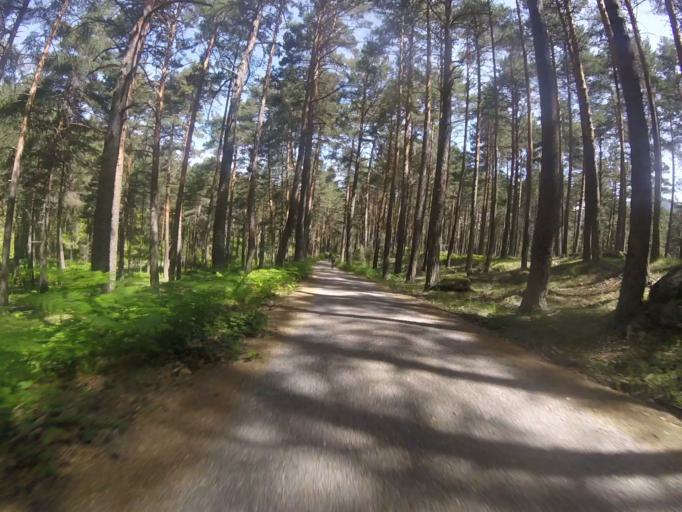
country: ES
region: Madrid
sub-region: Provincia de Madrid
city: Cercedilla
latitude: 40.8177
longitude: -4.0289
